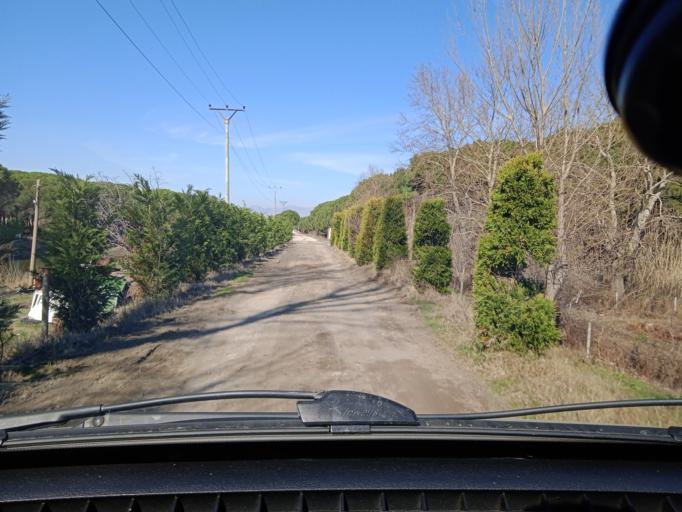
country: AL
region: Shkoder
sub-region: Rrethi i Shkodres
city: Velipoje
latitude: 41.8621
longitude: 19.4457
